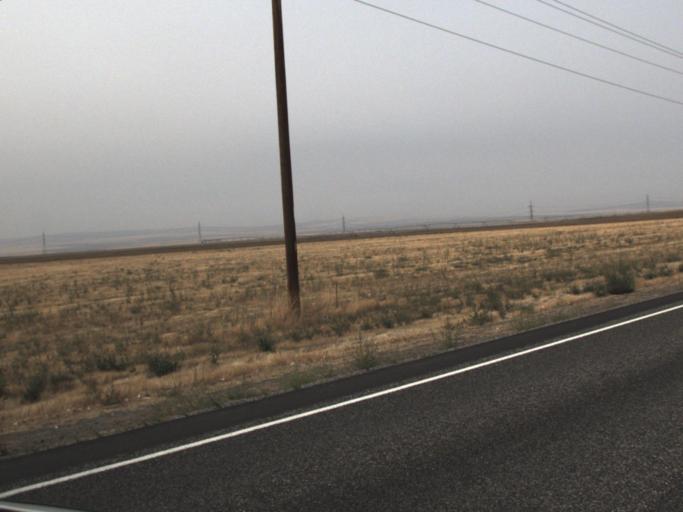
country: US
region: Oregon
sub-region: Morrow County
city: Irrigon
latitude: 46.0509
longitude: -119.6023
